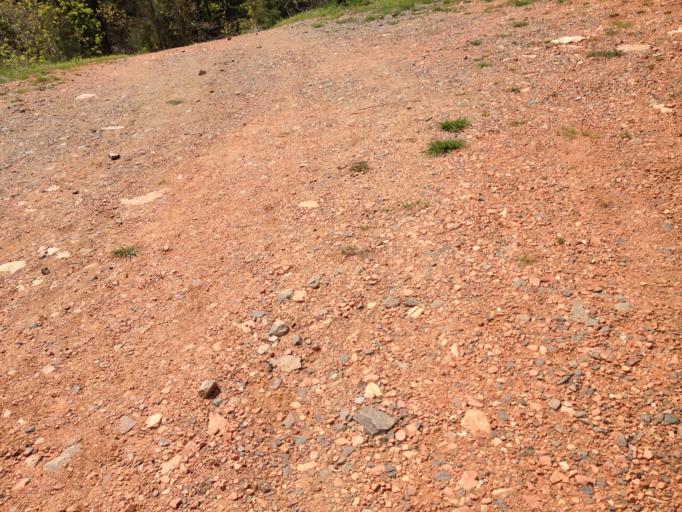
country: US
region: Colorado
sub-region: Boulder County
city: Boulder
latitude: 39.9249
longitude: -105.2784
